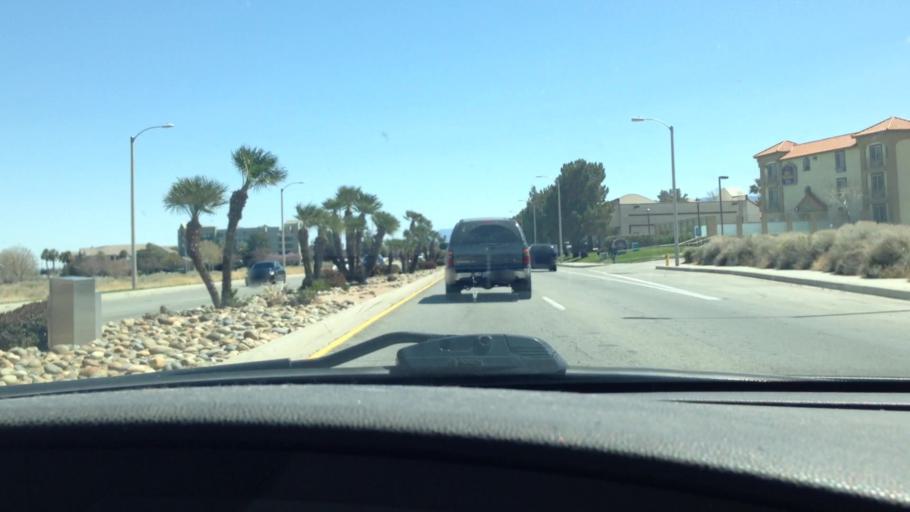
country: US
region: California
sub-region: Los Angeles County
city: Desert View Highlands
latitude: 34.5850
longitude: -118.1419
